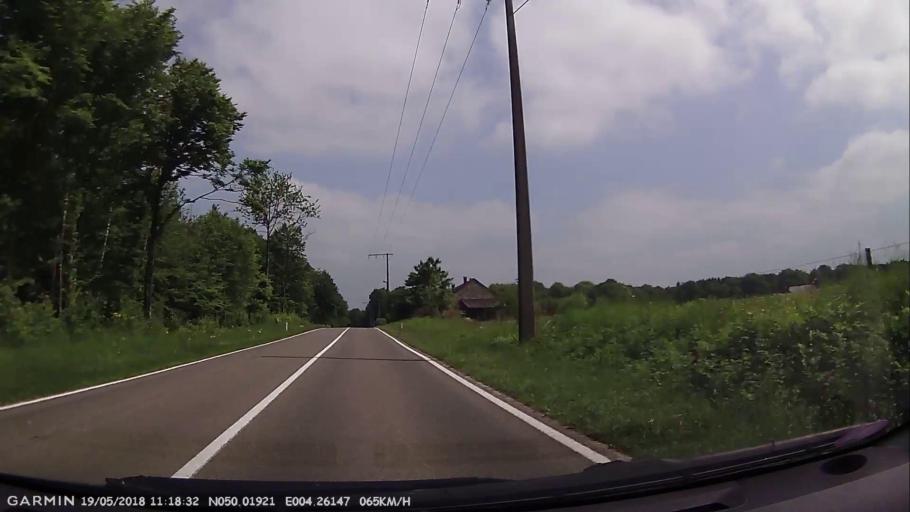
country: BE
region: Wallonia
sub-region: Province du Hainaut
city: Chimay
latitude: 50.0193
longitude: 4.2616
